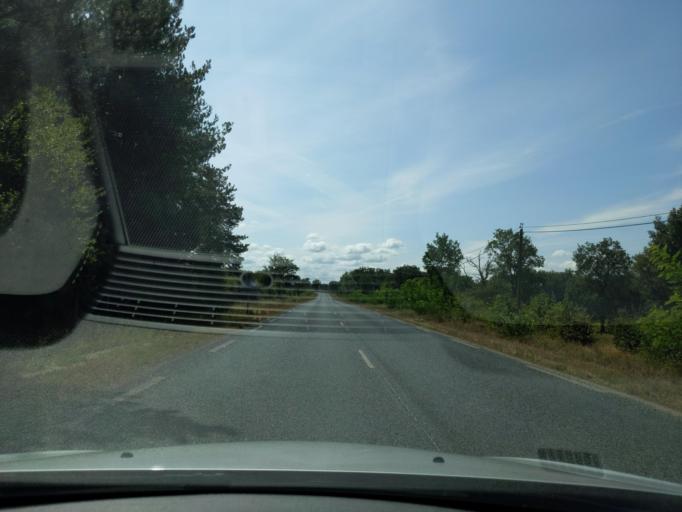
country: FR
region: Auvergne
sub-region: Departement de l'Allier
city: Doyet
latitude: 46.4507
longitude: 2.8171
